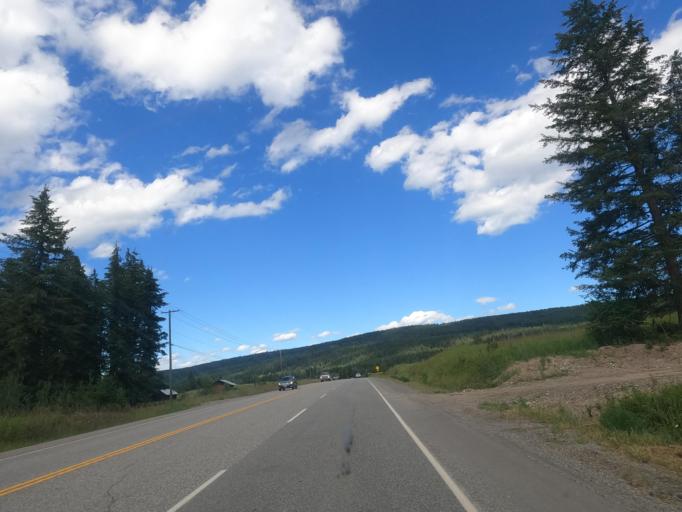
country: CA
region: British Columbia
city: Quesnel
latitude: 52.6145
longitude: -122.4602
